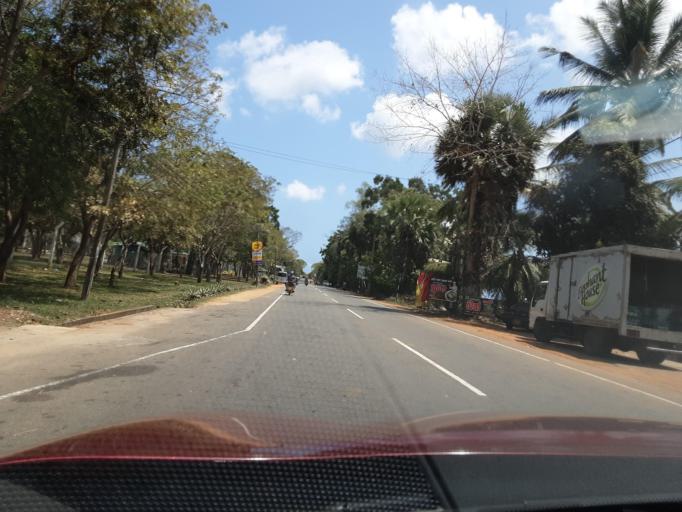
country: LK
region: Southern
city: Tangalla
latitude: 6.2547
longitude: 81.2272
